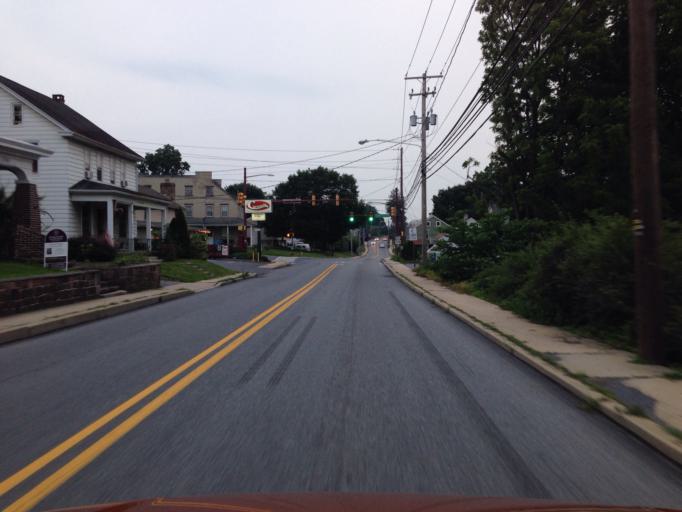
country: US
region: Pennsylvania
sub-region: Lancaster County
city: Rothsville
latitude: 40.1515
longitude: -76.2501
